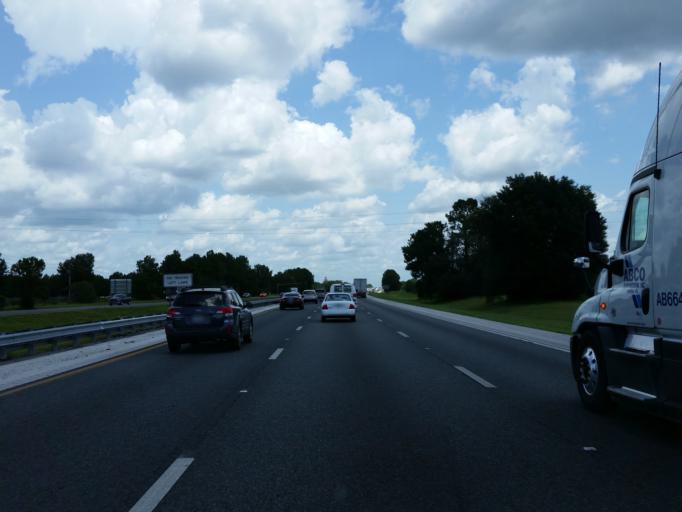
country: US
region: Florida
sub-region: Marion County
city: Belleview
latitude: 29.0096
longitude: -82.1523
